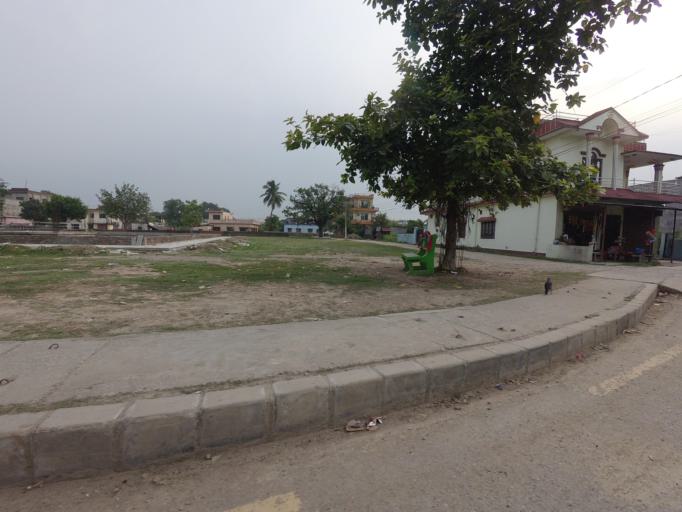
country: NP
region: Western Region
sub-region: Lumbini Zone
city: Bhairahawa
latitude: 27.5200
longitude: 83.4430
